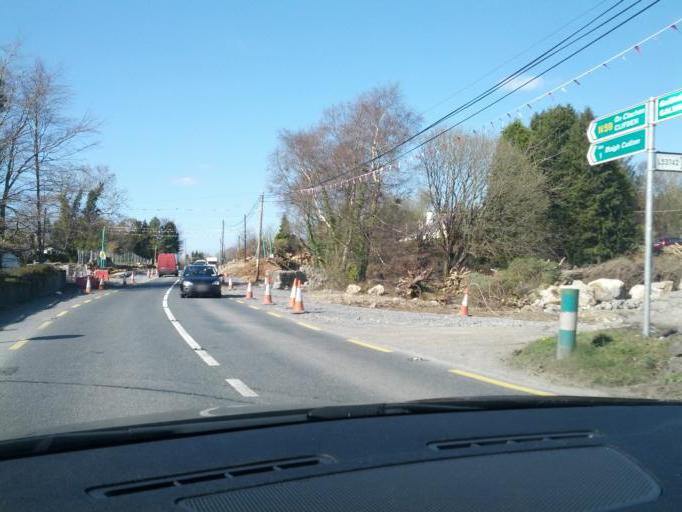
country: IE
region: Connaught
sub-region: County Galway
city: Moycullen
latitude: 53.3262
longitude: -9.1674
